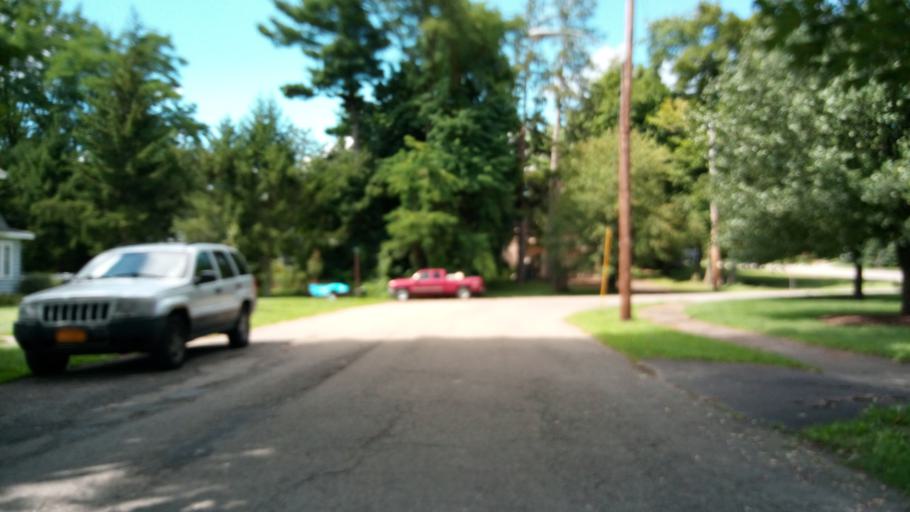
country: US
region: New York
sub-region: Chemung County
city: West Elmira
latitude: 42.0789
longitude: -76.8321
